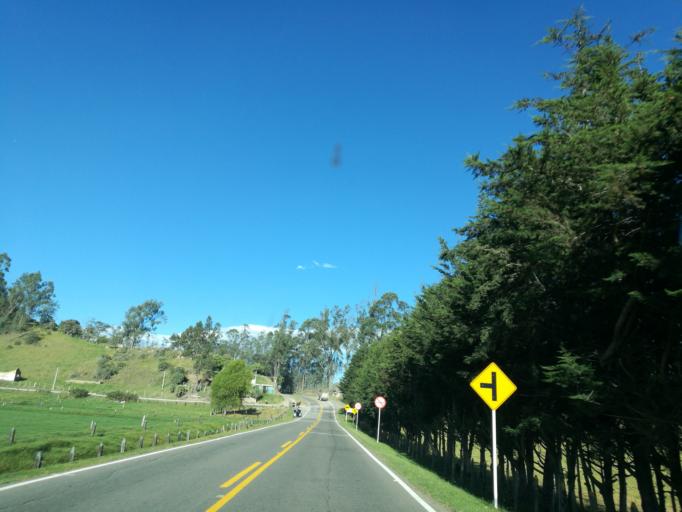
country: CO
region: Boyaca
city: Chiquinquira
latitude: 5.6232
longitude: -73.7691
